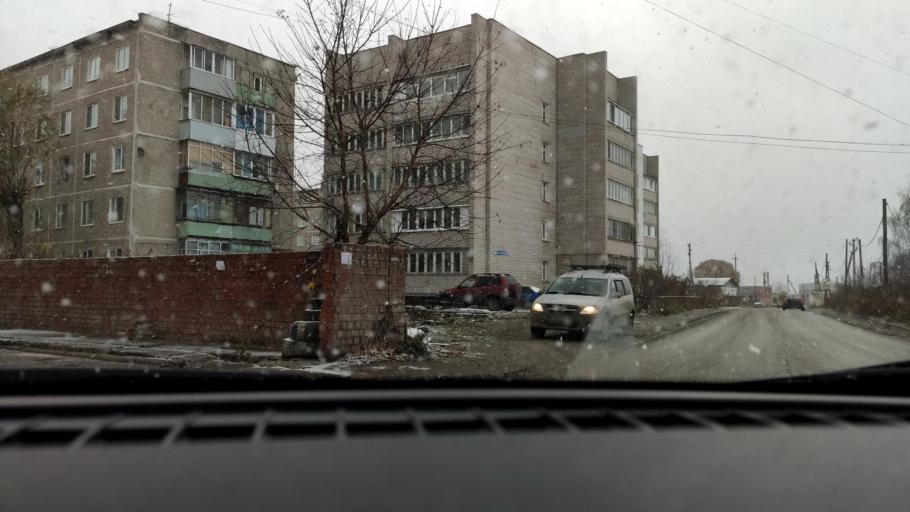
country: RU
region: Perm
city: Kondratovo
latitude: 57.9474
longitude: 56.0808
